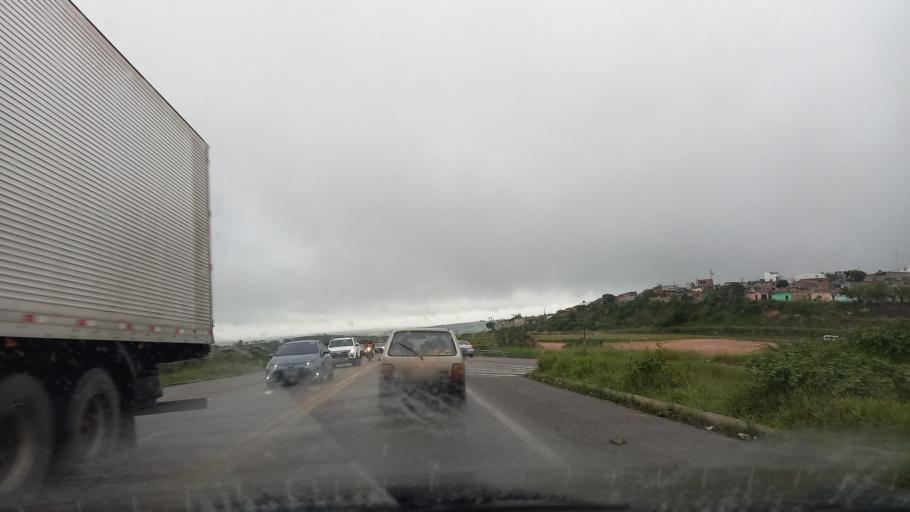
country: BR
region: Pernambuco
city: Garanhuns
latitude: -8.8772
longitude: -36.5084
